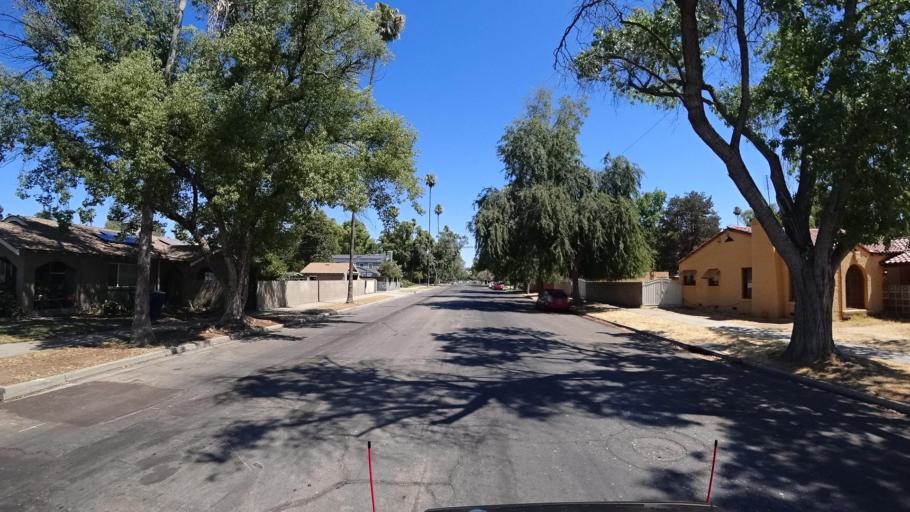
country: US
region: California
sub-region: Fresno County
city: Fresno
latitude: 36.7382
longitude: -119.7627
